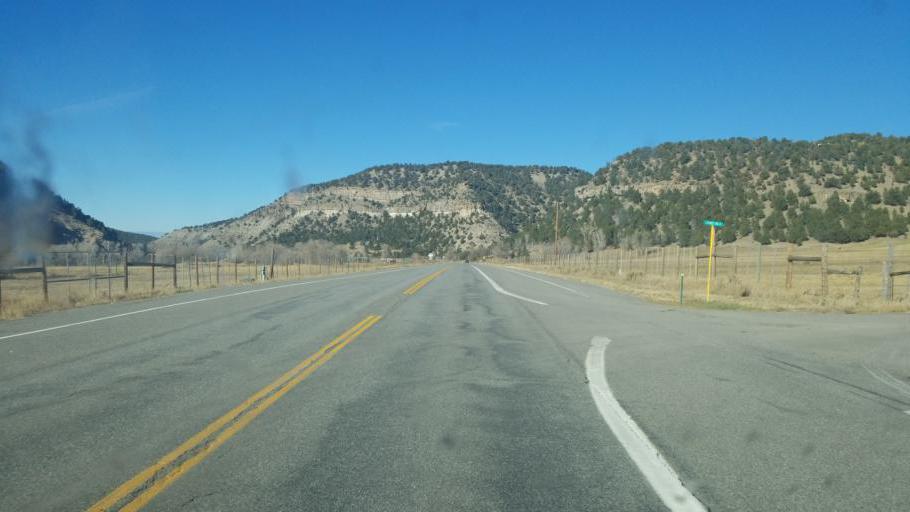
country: US
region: Colorado
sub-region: Ouray County
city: Ouray
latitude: 38.2556
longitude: -107.7575
